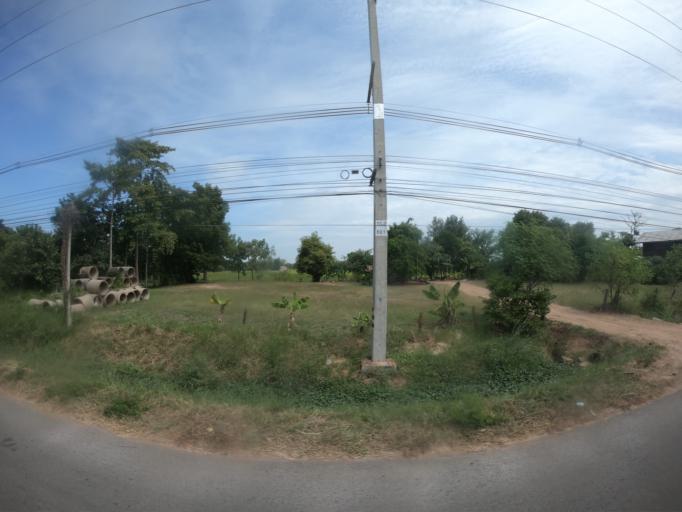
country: TH
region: Maha Sarakham
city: Chiang Yuen
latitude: 16.4183
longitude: 103.0791
